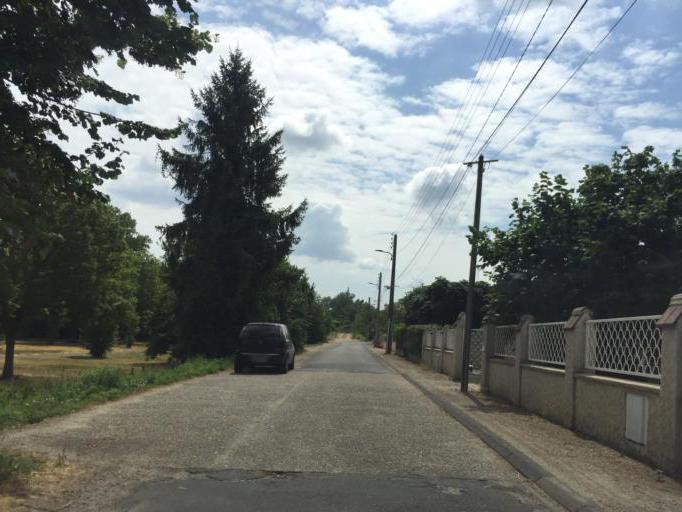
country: FR
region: Auvergne
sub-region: Departement de l'Allier
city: Moulins
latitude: 46.5568
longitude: 3.3244
